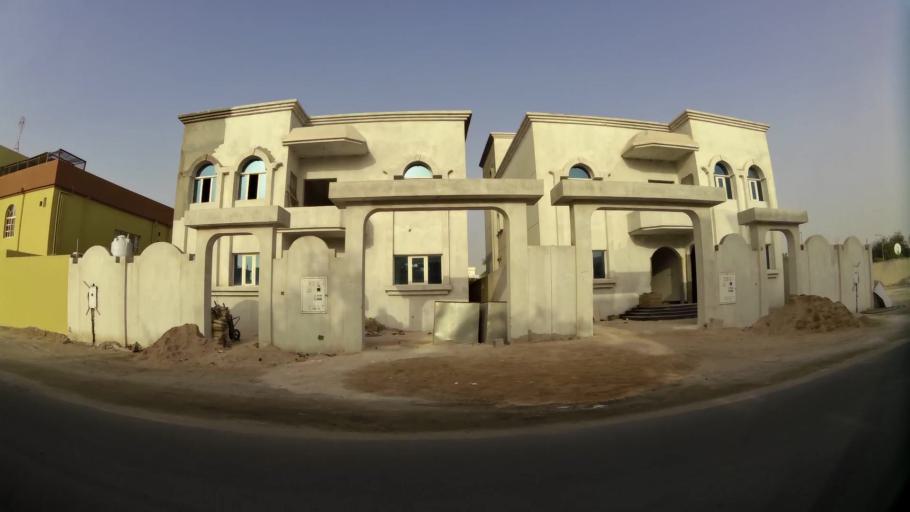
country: QA
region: Baladiyat ar Rayyan
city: Ar Rayyan
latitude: 25.2522
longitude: 51.4472
